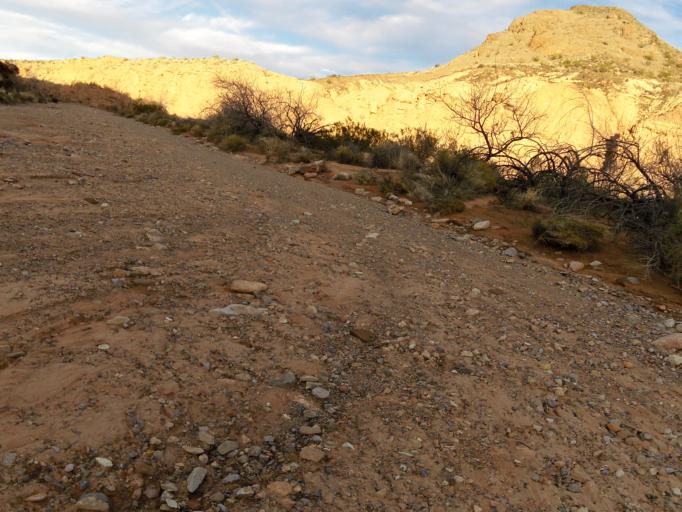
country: US
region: Nevada
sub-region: Clark County
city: Boulder City
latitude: 36.2409
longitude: -114.6329
